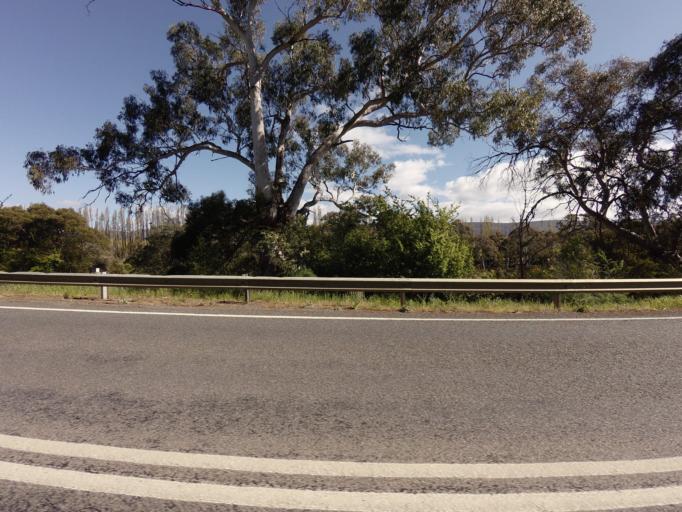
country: AU
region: Tasmania
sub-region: Derwent Valley
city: New Norfolk
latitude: -42.7359
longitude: 146.9547
